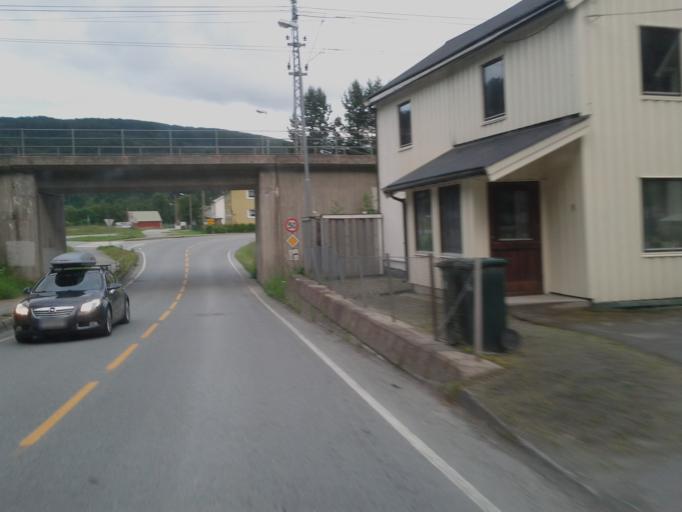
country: NO
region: Sor-Trondelag
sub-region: Midtre Gauldal
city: Storen
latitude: 63.0466
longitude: 10.2821
